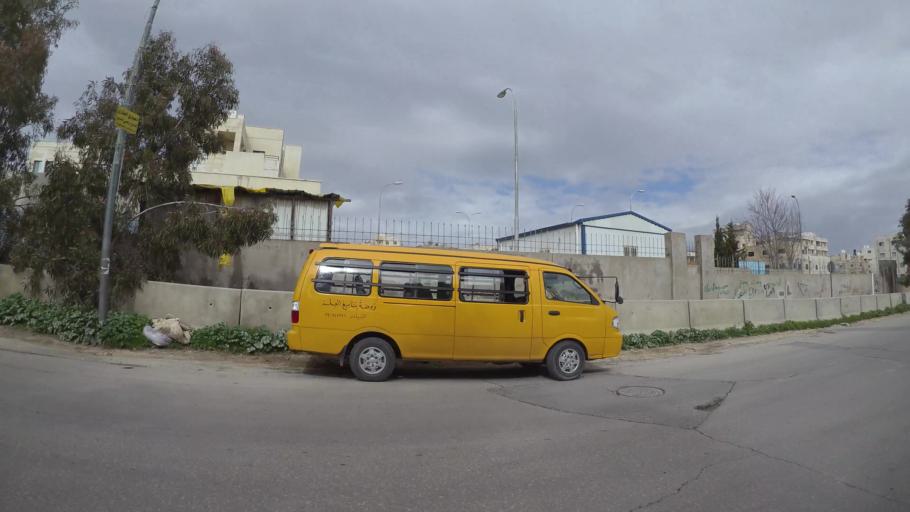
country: JO
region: Amman
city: Wadi as Sir
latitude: 31.9484
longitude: 35.8327
